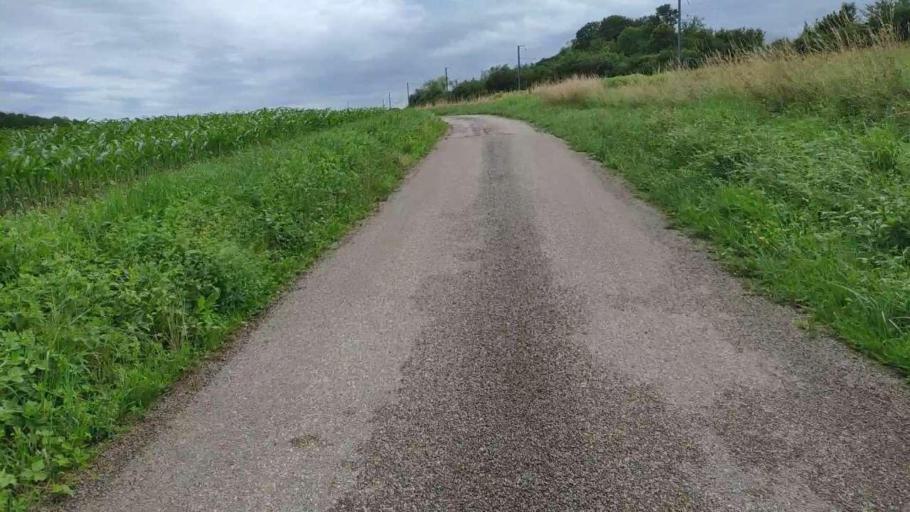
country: FR
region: Franche-Comte
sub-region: Departement du Jura
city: Poligny
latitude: 46.8064
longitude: 5.6054
